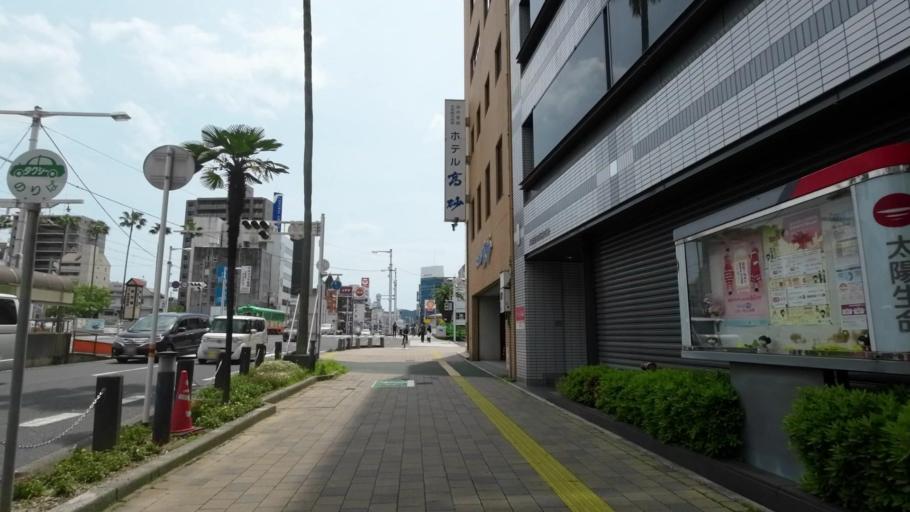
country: JP
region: Kochi
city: Kochi-shi
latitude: 33.5645
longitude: 133.5433
